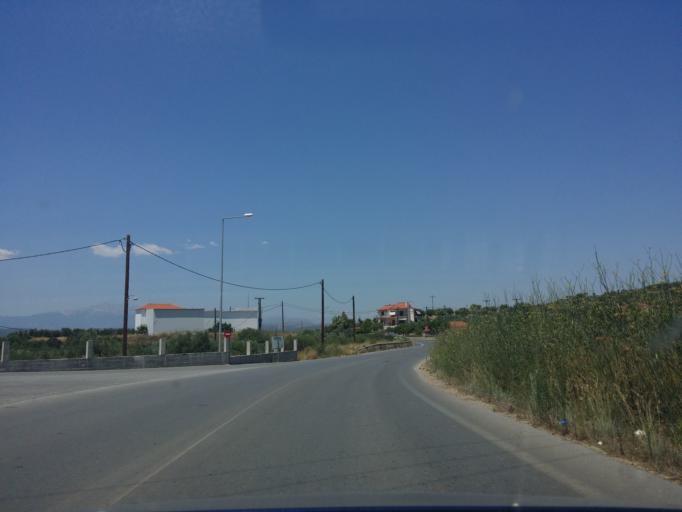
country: GR
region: Peloponnese
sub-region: Nomos Lakonias
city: Vlakhiotis
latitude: 36.8600
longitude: 22.7209
